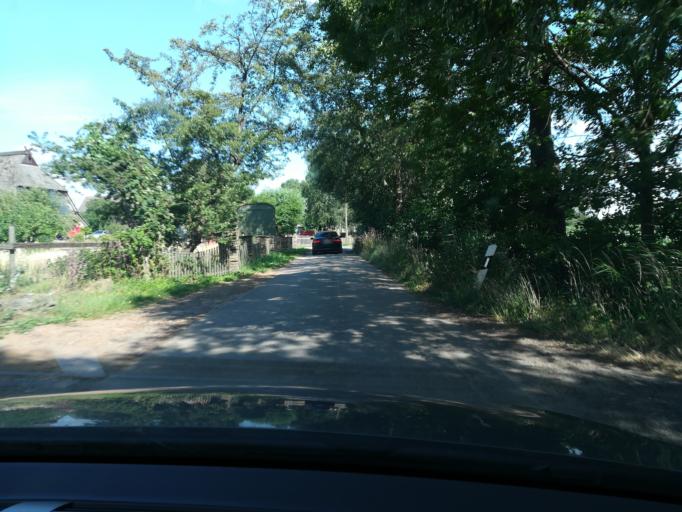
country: DE
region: Hamburg
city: Rothenburgsort
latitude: 53.4914
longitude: 10.0424
